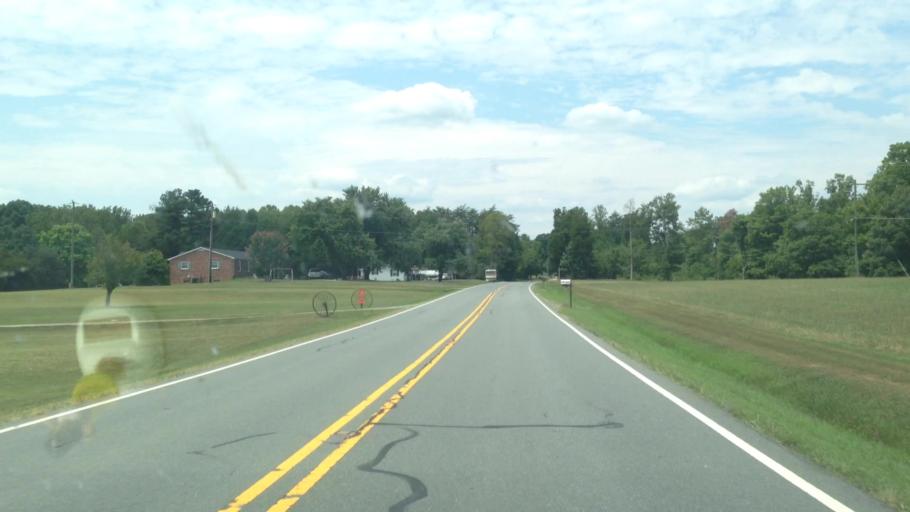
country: US
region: North Carolina
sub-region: Stokes County
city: Walnut Cove
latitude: 36.3574
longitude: -80.0621
